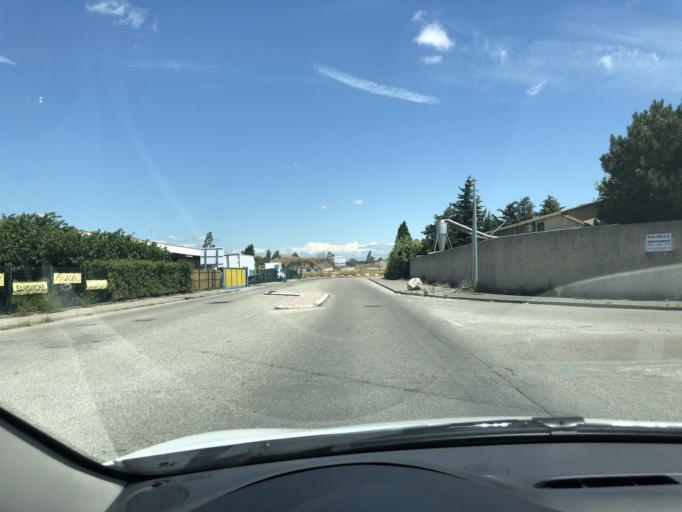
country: FR
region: Provence-Alpes-Cote d'Azur
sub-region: Departement des Bouches-du-Rhone
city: Chateaurenard
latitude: 43.8971
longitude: 4.8789
